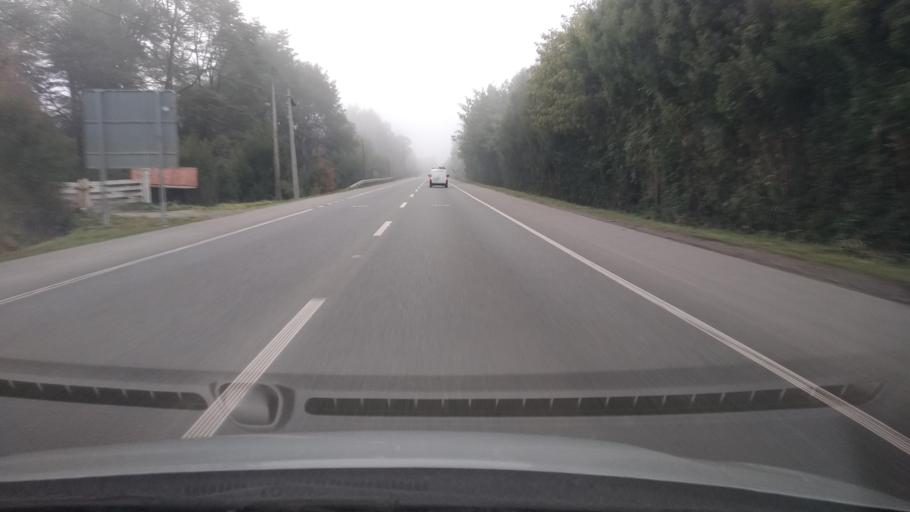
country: CL
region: Los Lagos
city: Las Animas
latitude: -39.7557
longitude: -73.2287
